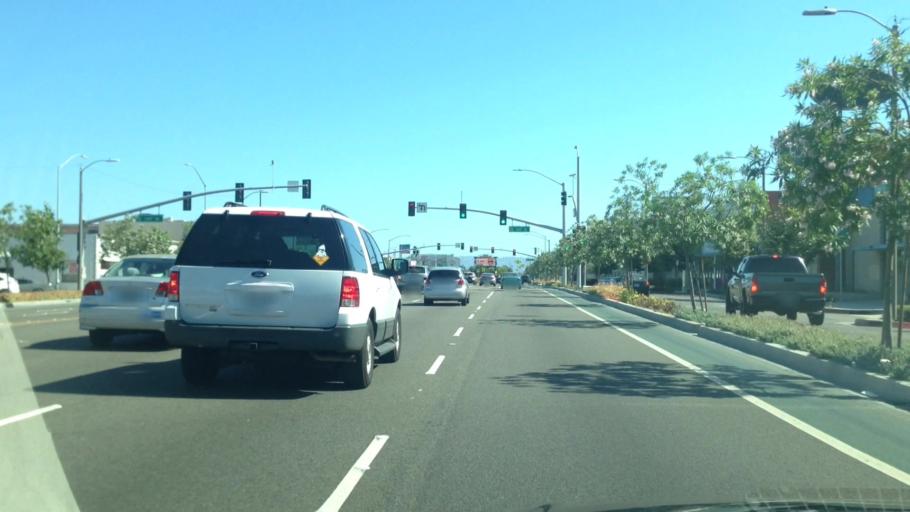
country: US
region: California
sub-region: Los Angeles County
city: Hawthorne
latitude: 33.9149
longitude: -118.3527
